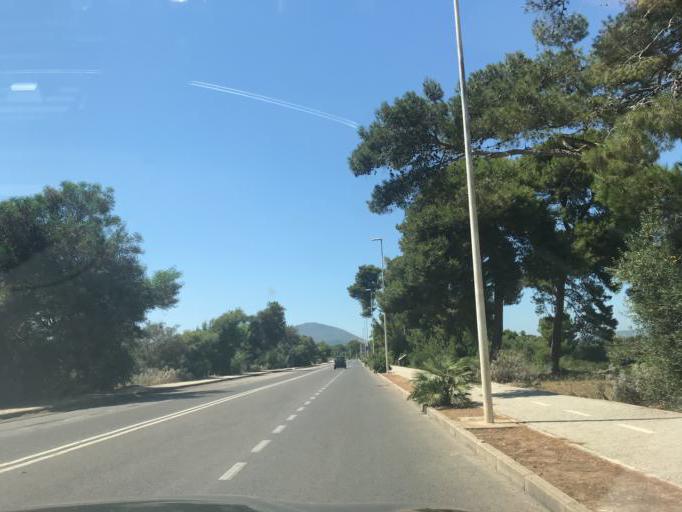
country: IT
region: Sardinia
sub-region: Provincia di Sassari
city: Alghero
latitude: 40.5884
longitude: 8.3112
